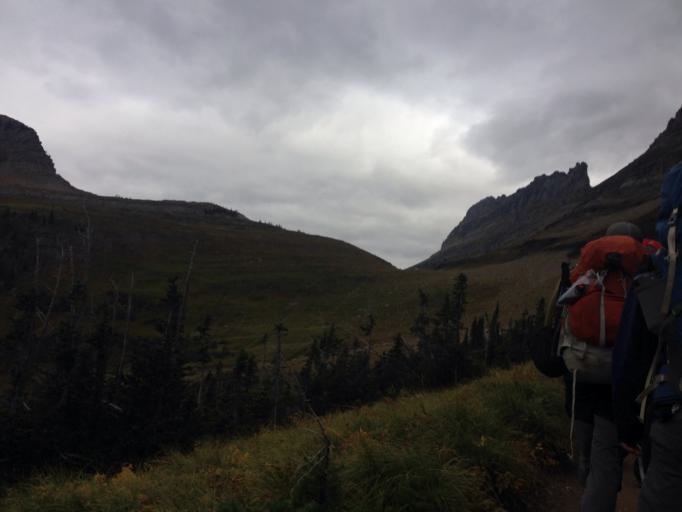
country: US
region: Montana
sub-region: Flathead County
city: Columbia Falls
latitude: 48.7306
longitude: -113.7198
